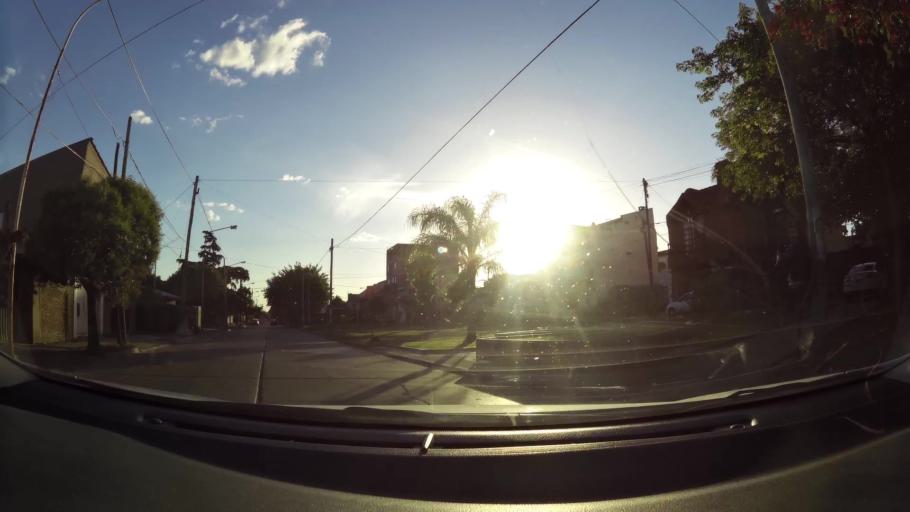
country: AR
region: Buenos Aires F.D.
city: Villa Lugano
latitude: -34.6944
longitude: -58.4818
